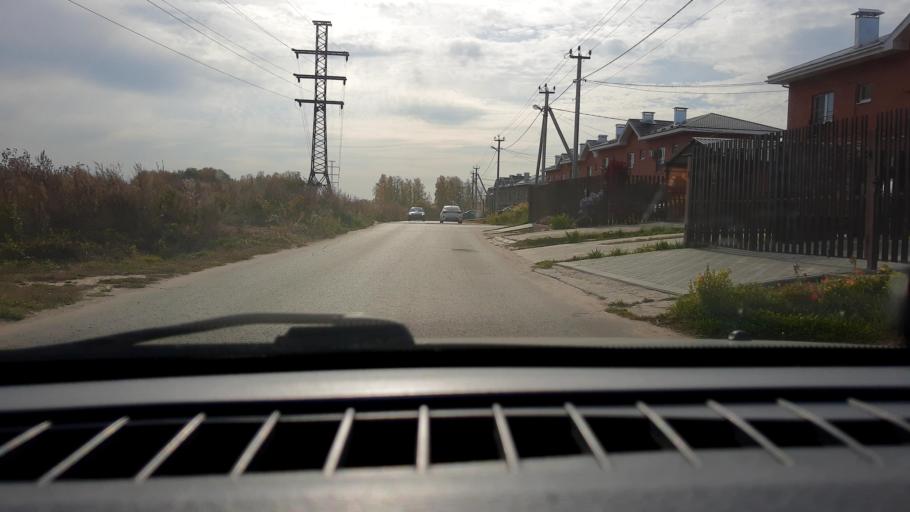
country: RU
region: Nizjnij Novgorod
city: Afonino
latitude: 56.2165
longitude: 44.0910
